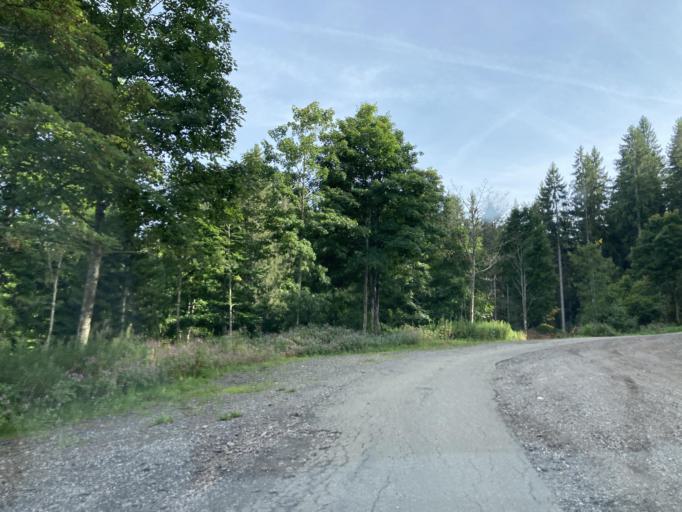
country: DE
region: Baden-Wuerttemberg
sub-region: Freiburg Region
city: Furtwangen im Schwarzwald
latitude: 47.9978
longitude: 8.1951
